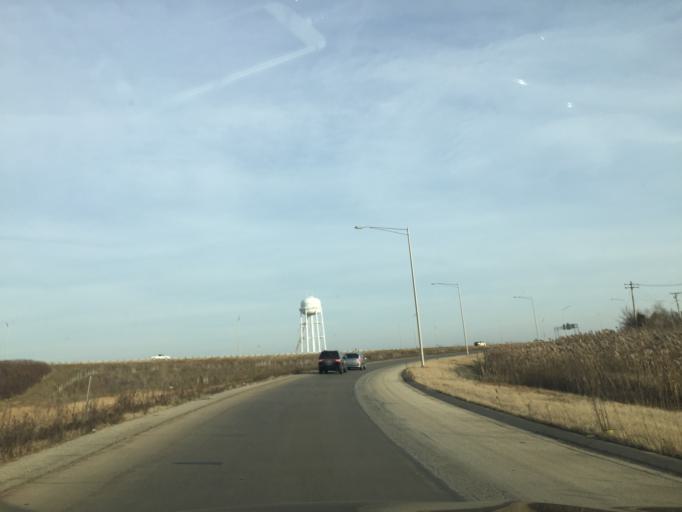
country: US
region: Illinois
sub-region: Will County
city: Bolingbrook
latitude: 41.7013
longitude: -88.0345
